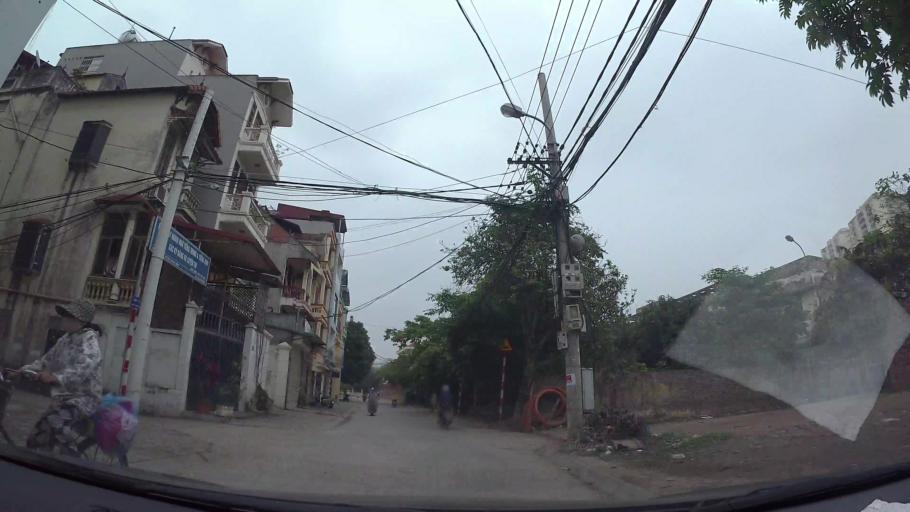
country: VN
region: Ha Noi
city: Hai BaTrung
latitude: 20.9947
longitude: 105.8853
